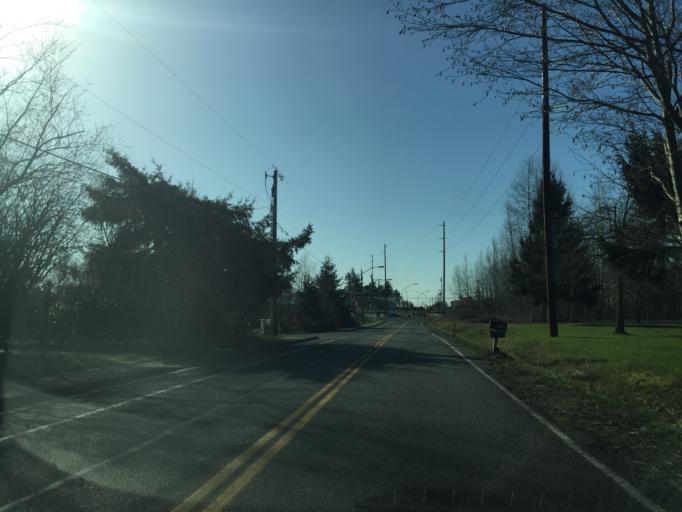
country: US
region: Washington
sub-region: Whatcom County
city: Bellingham
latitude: 48.7925
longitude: -122.5080
